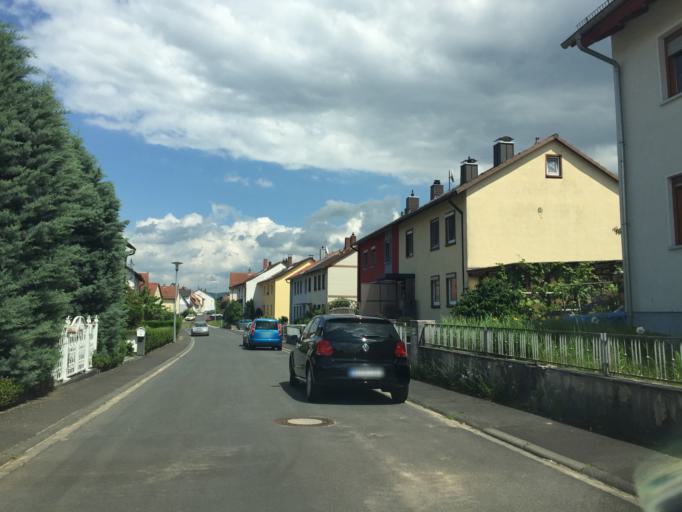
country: DE
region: Bavaria
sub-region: Regierungsbezirk Unterfranken
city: Goldbach
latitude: 49.9889
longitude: 9.1808
